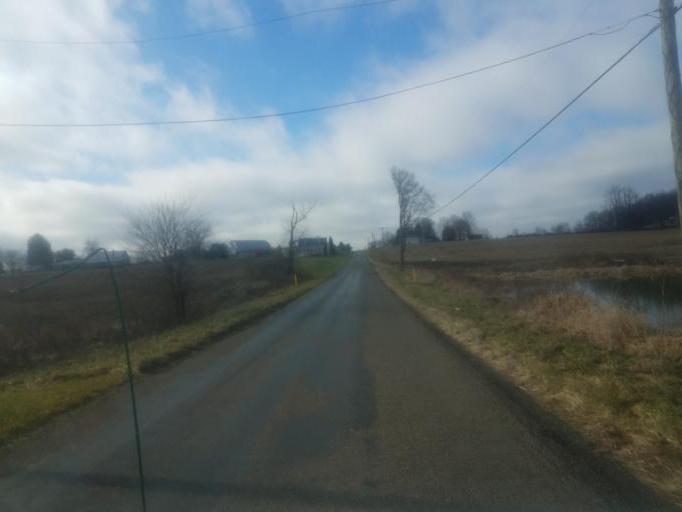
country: US
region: Ohio
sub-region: Richland County
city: Lexington
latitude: 40.6668
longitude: -82.5539
